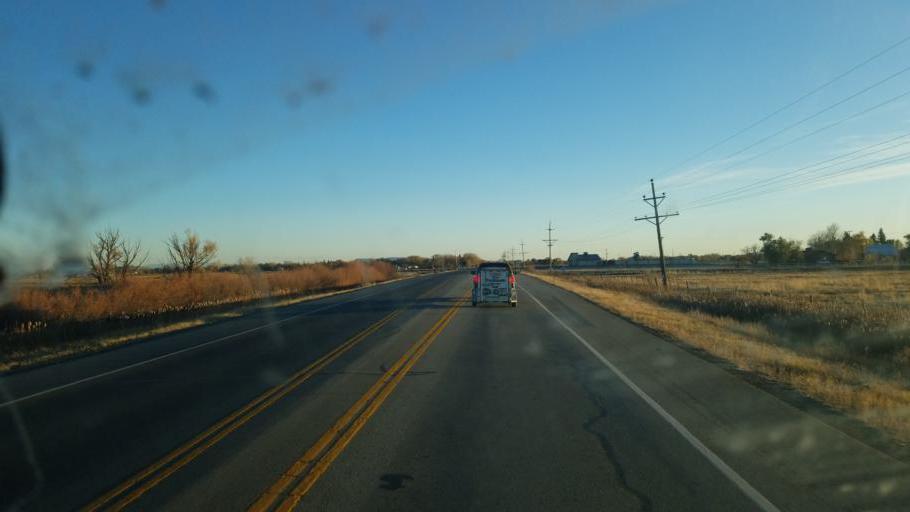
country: US
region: Colorado
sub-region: Alamosa County
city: Alamosa East
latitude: 37.4926
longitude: -105.8576
